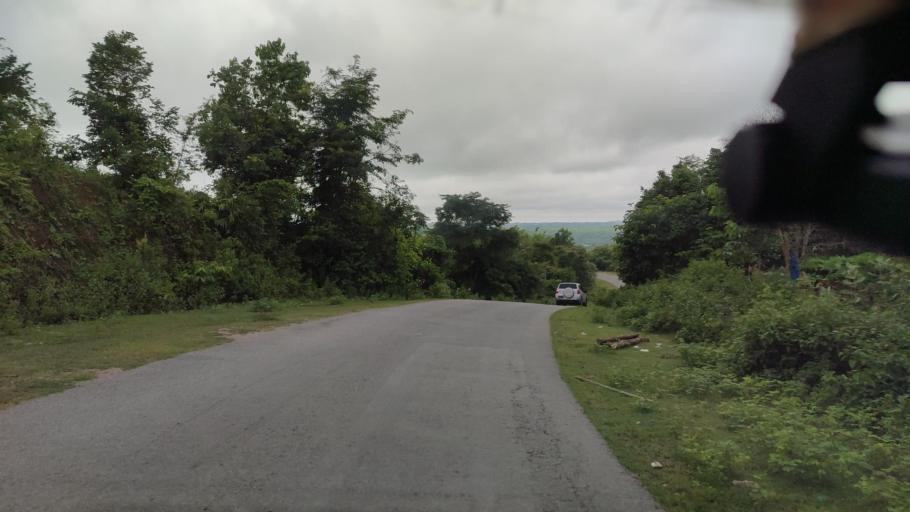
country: MM
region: Mandalay
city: Nay Pyi Taw
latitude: 19.9982
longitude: 95.9207
